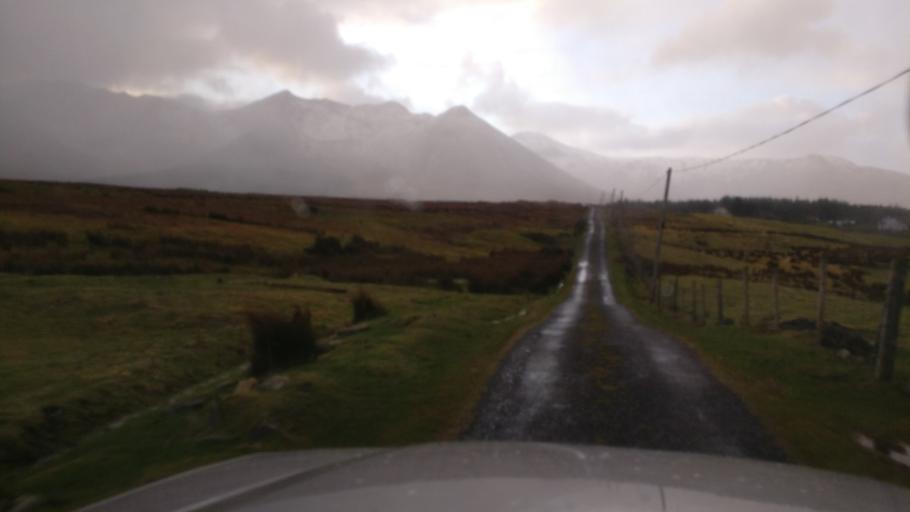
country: IE
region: Connaught
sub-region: County Galway
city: Clifden
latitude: 53.5180
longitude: -9.7248
